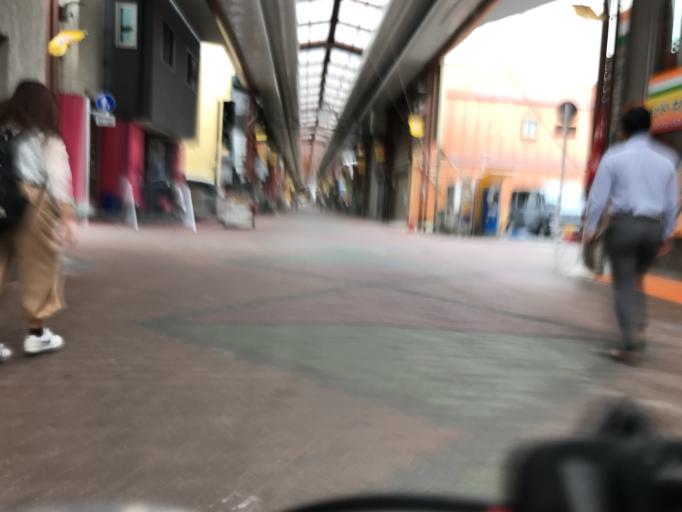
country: JP
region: Aichi
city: Nagoya-shi
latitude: 35.1764
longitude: 136.8896
